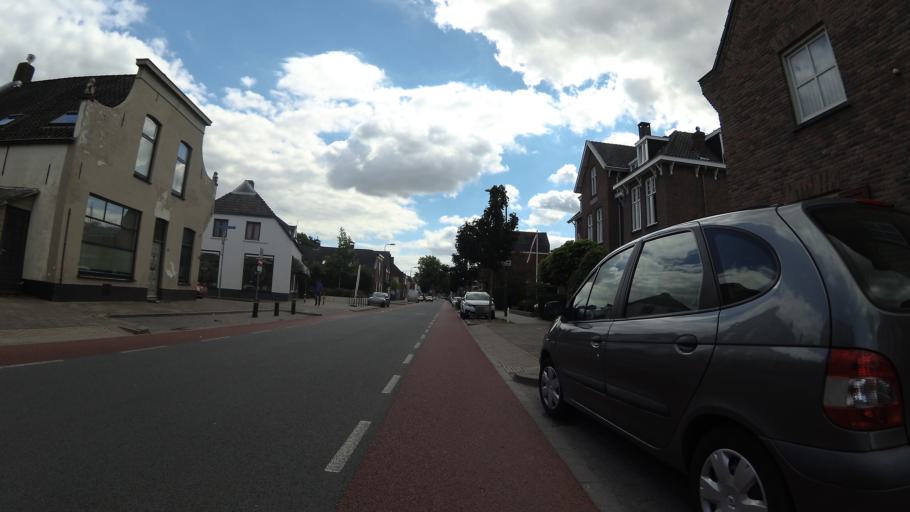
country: NL
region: North Brabant
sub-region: Gemeente Waalwijk
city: Waalwijk
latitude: 51.6590
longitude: 5.0353
